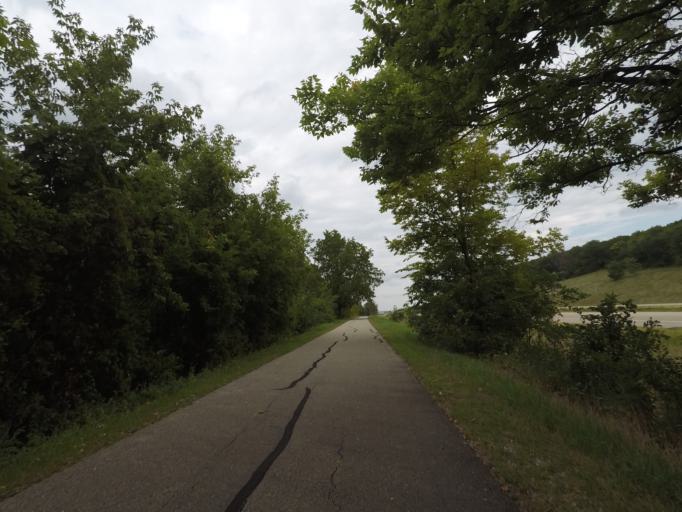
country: US
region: Wisconsin
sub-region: Jefferson County
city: Lake Koshkonong
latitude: 42.8788
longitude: -88.8829
